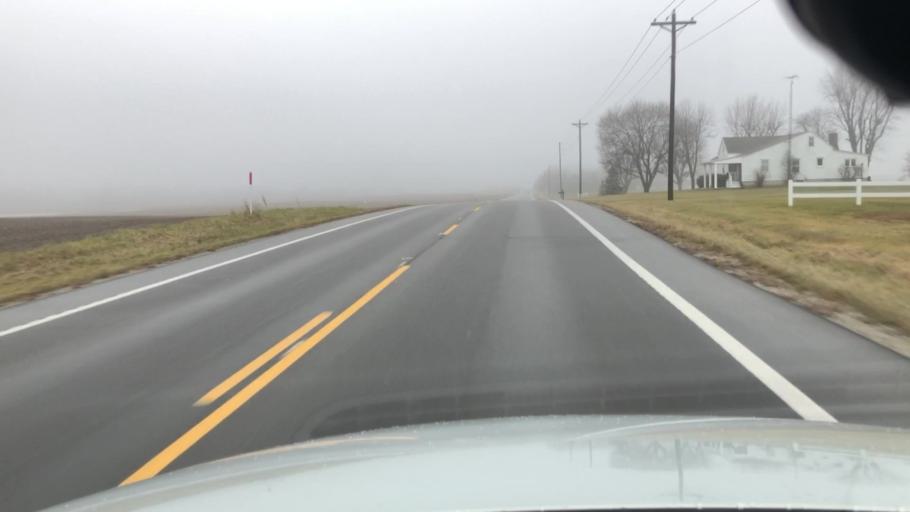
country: US
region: Ohio
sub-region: Logan County
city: Lakeview
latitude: 40.6214
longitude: -83.9046
